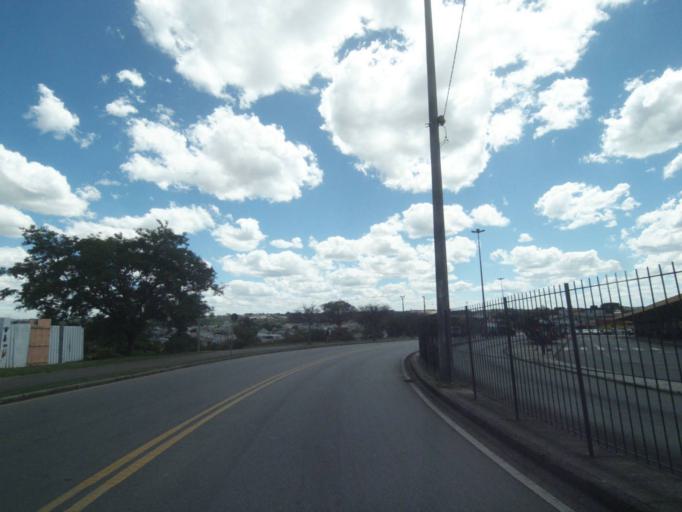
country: BR
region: Parana
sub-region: Curitiba
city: Curitiba
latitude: -25.5120
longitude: -49.3240
